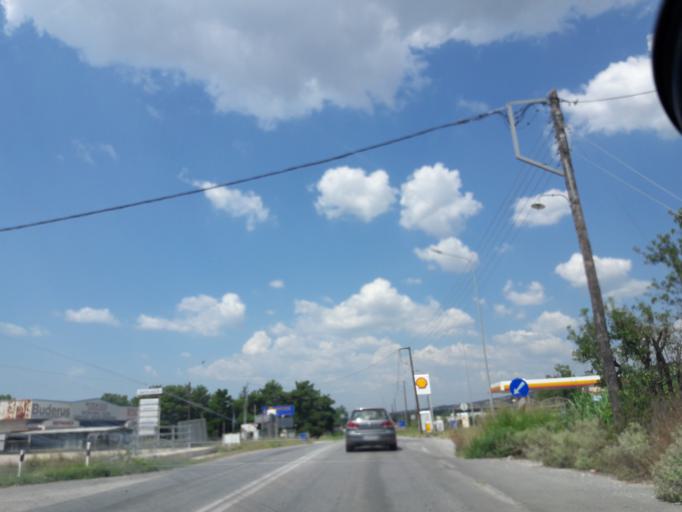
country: GR
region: Central Macedonia
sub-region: Nomos Thessalonikis
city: Souroti
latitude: 40.5043
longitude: 23.0922
